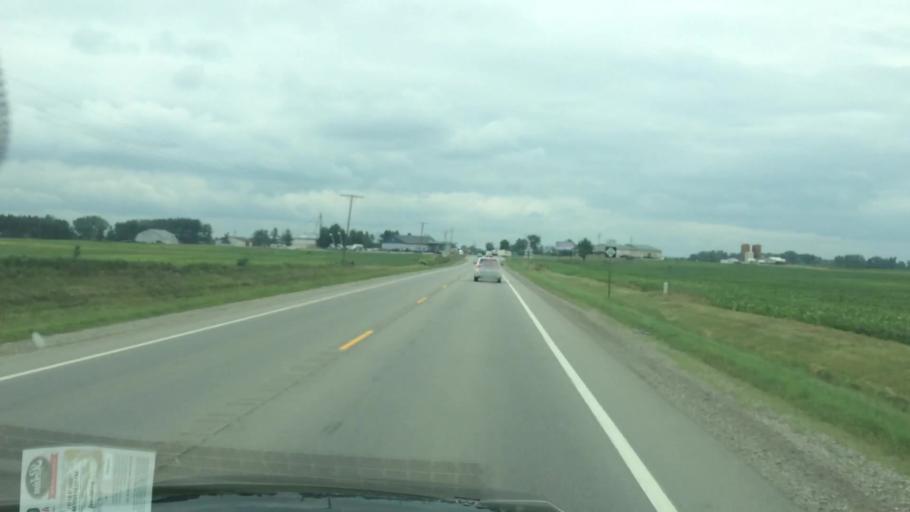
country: US
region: Michigan
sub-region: Sanilac County
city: Marlette
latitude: 43.4109
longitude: -83.0870
